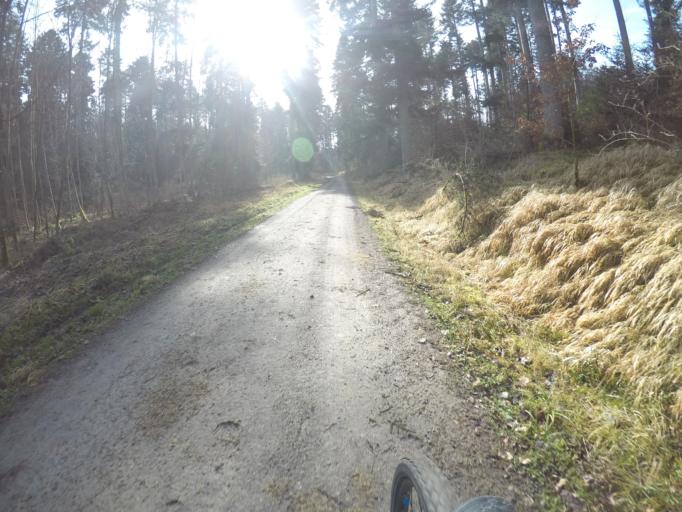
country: DE
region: Baden-Wuerttemberg
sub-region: Regierungsbezirk Stuttgart
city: Oberjettingen
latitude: 48.5909
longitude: 8.7952
